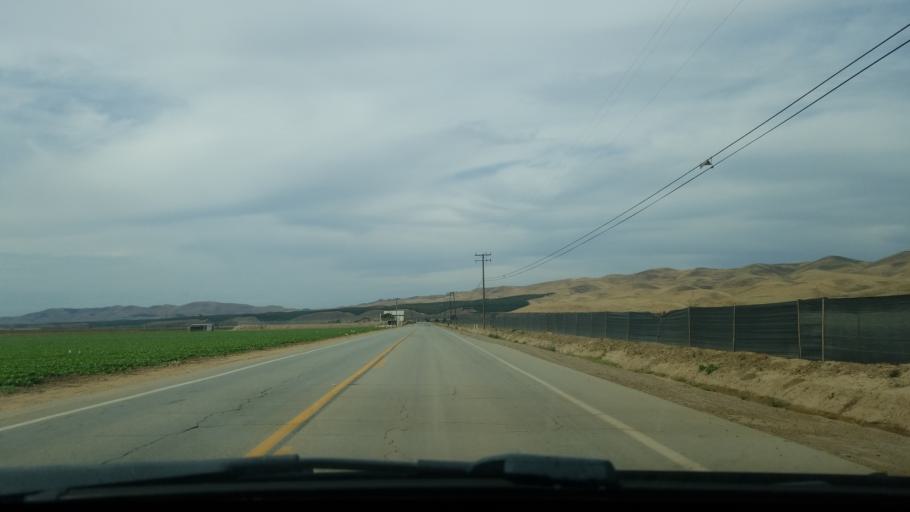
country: US
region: California
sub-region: Santa Barbara County
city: Santa Maria
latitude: 34.9134
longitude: -120.3478
